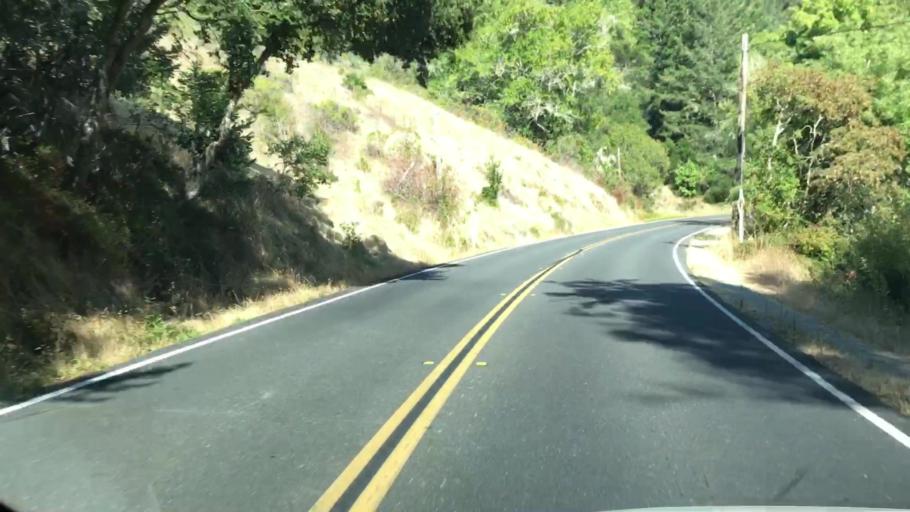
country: US
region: California
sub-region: Marin County
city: Lagunitas-Forest Knolls
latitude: 38.0305
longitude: -122.7388
